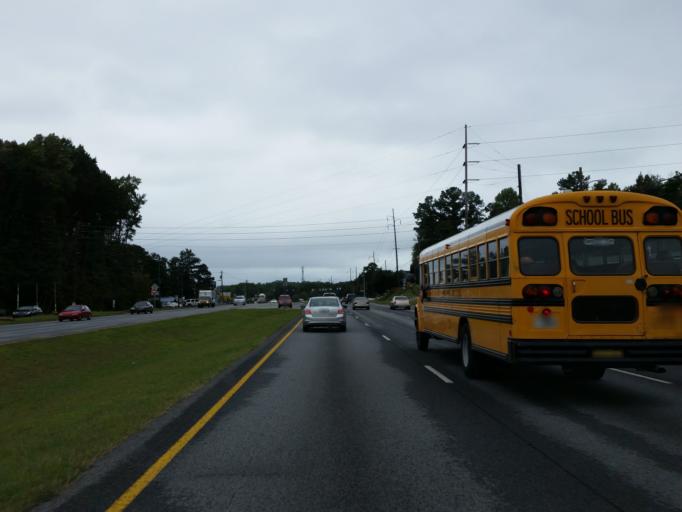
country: US
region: Georgia
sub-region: Clayton County
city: Jonesboro
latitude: 33.5507
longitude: -84.3701
